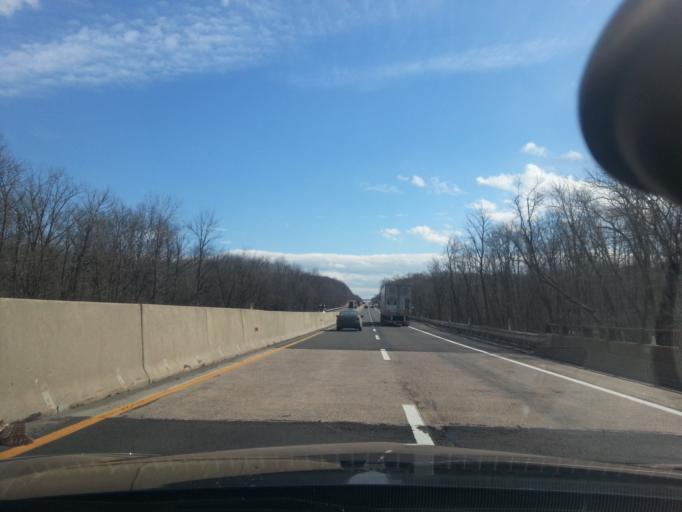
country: US
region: Pennsylvania
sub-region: Montgomery County
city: Woxall
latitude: 40.3701
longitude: -75.4016
